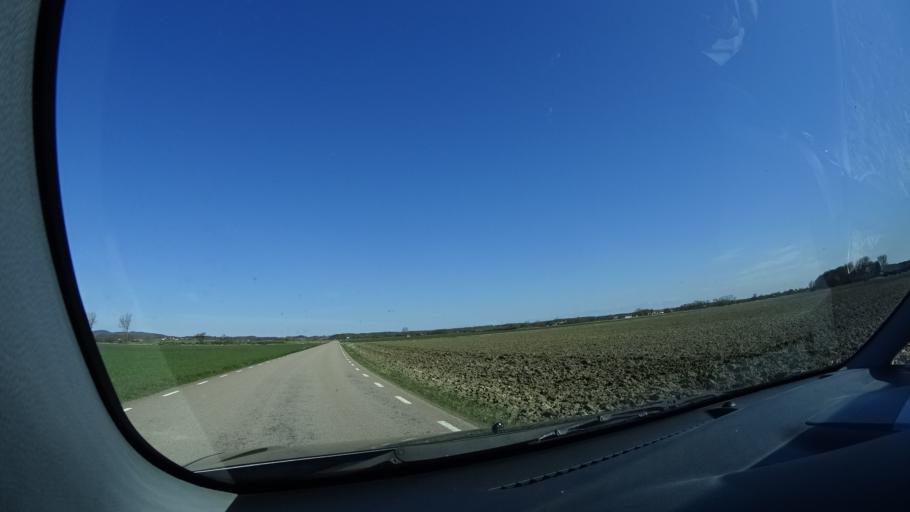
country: SE
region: Skane
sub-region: Hoganas Kommun
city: Hoganas
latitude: 56.2308
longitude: 12.5862
